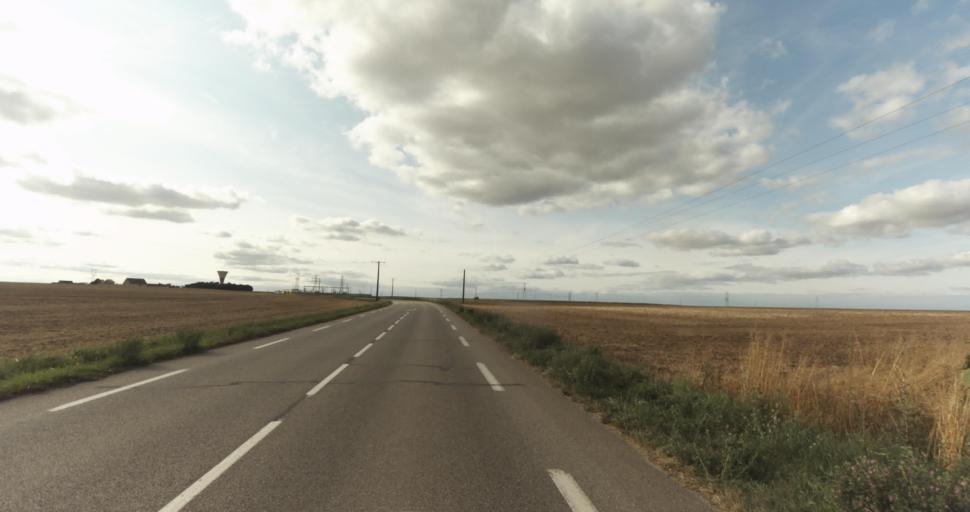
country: FR
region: Haute-Normandie
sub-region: Departement de l'Eure
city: Ivry-la-Bataille
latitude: 48.8885
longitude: 1.4433
